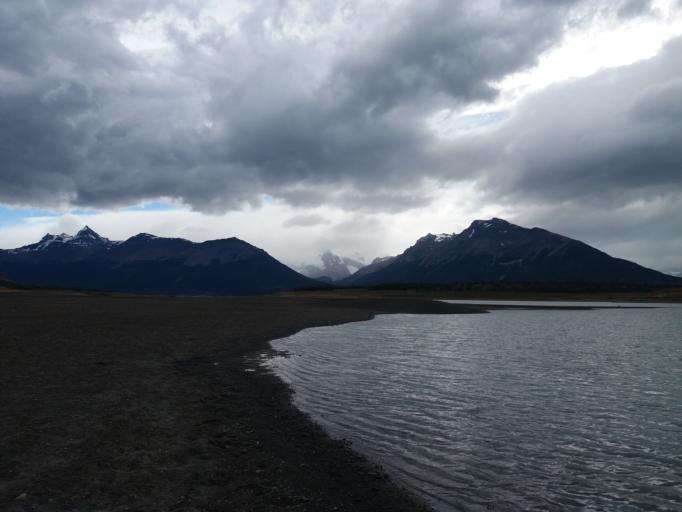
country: AR
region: Santa Cruz
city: El Calafate
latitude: -50.5533
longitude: -72.8530
